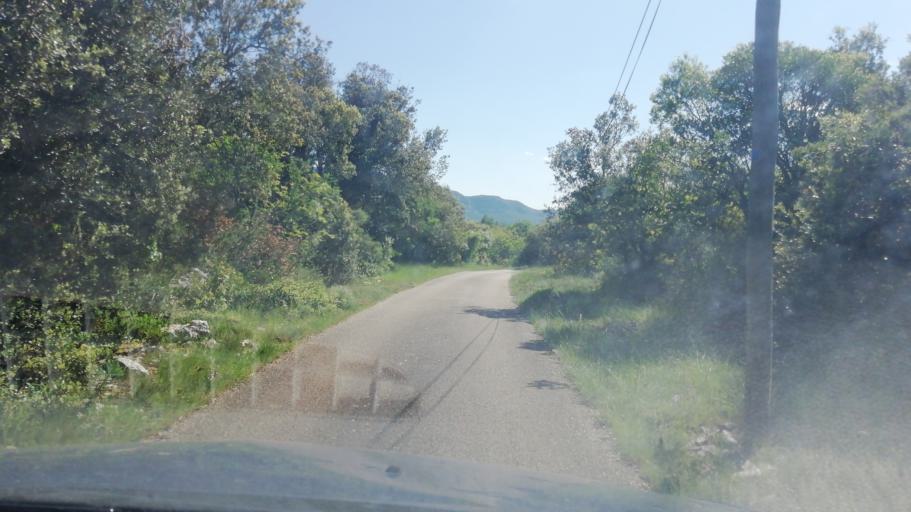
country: FR
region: Languedoc-Roussillon
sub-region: Departement de l'Herault
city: Saint-Mathieu-de-Treviers
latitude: 43.8317
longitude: 3.8208
